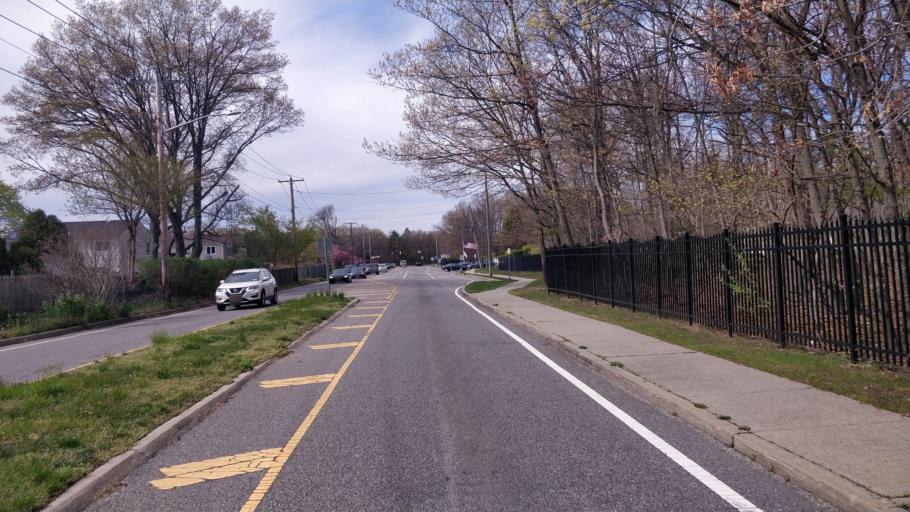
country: US
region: New York
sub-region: Suffolk County
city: Terryville
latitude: 40.8970
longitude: -73.0800
